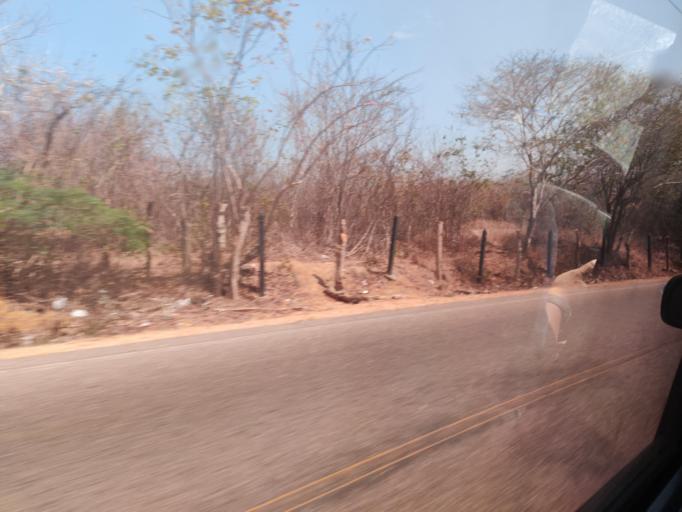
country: CO
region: Bolivar
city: Turbana
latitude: 10.2221
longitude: -75.5816
